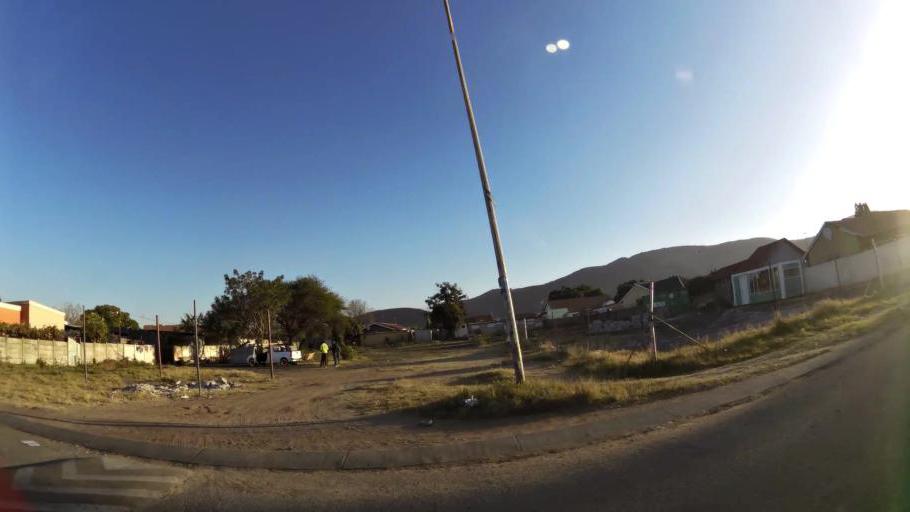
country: ZA
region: North-West
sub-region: Bojanala Platinum District Municipality
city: Rustenburg
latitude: -25.6434
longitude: 27.2104
